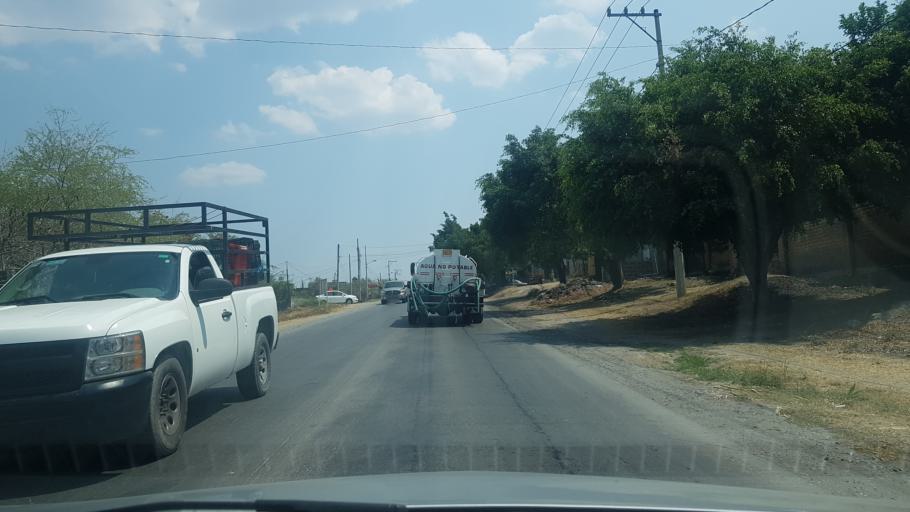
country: MX
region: Morelos
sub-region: Tlaltizapan de Zapata
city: Colonia Palo Prieto (Chipitongo)
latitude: 18.7120
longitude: -99.1177
